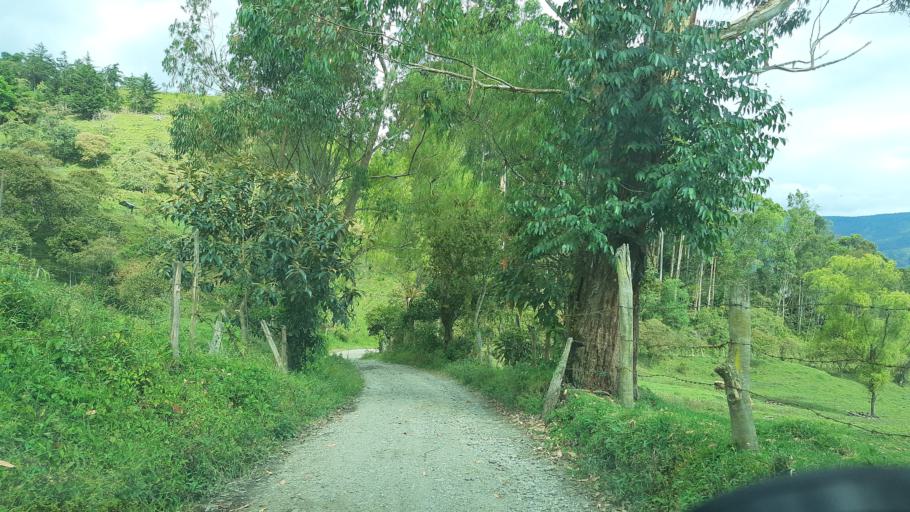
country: CO
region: Boyaca
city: Garagoa
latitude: 5.0466
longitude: -73.3487
